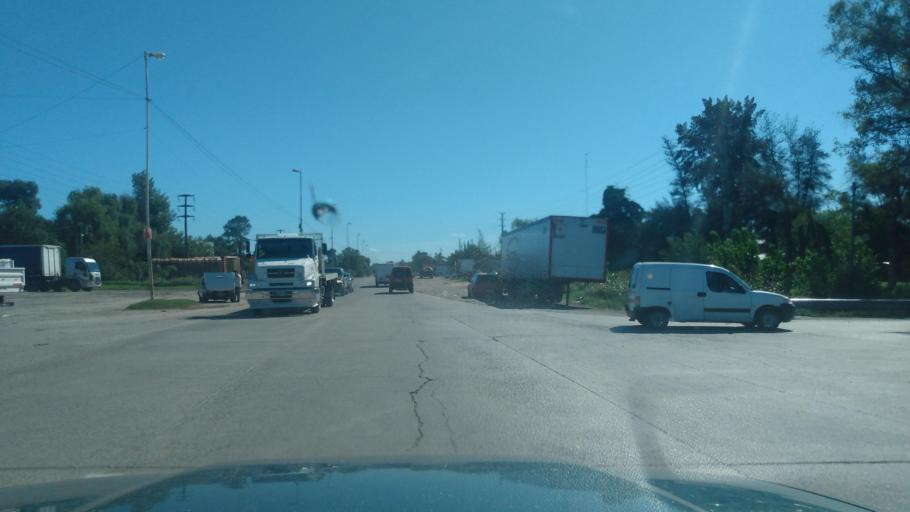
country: AR
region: Buenos Aires
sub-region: Partido de General Rodriguez
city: General Rodriguez
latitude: -34.5920
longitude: -58.9472
